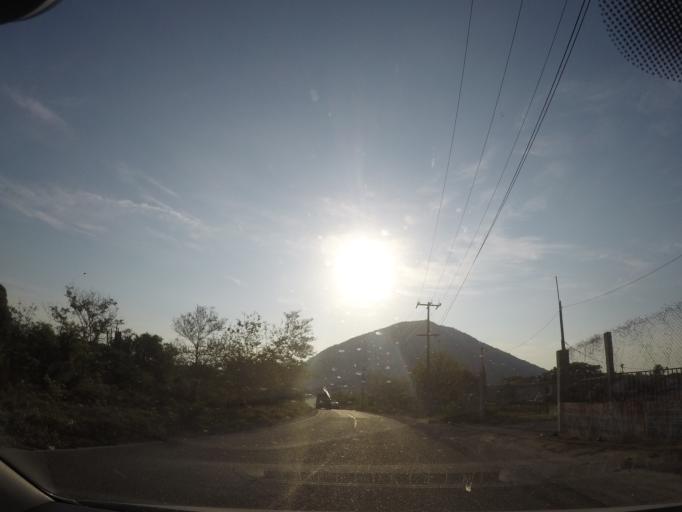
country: MX
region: Oaxaca
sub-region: Santo Domingo Tehuantepec
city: La Noria
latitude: 16.2369
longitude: -95.1611
